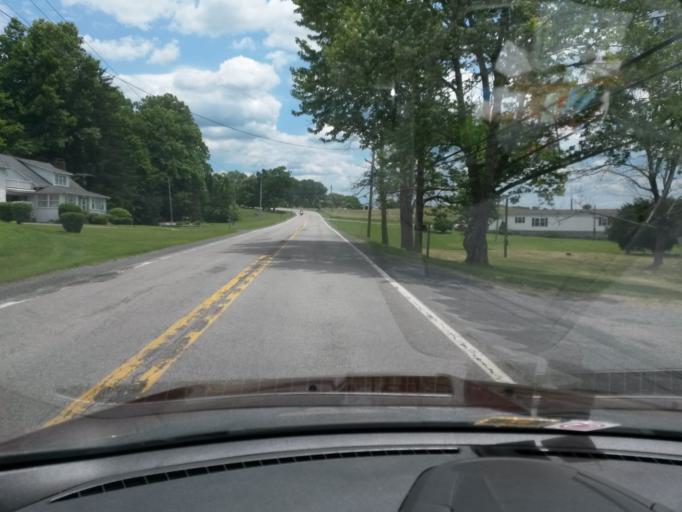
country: US
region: West Virginia
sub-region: Nicholas County
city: Summersville
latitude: 38.2600
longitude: -80.7879
